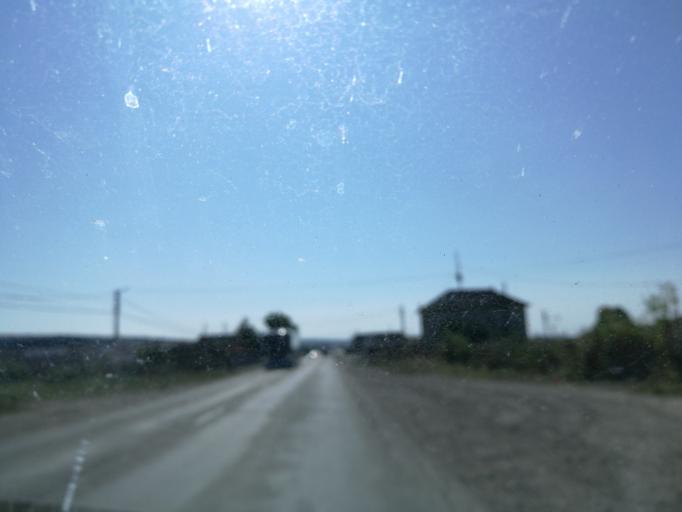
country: RO
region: Iasi
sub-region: Comuna Motca
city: Motca
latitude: 47.2377
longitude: 26.5859
